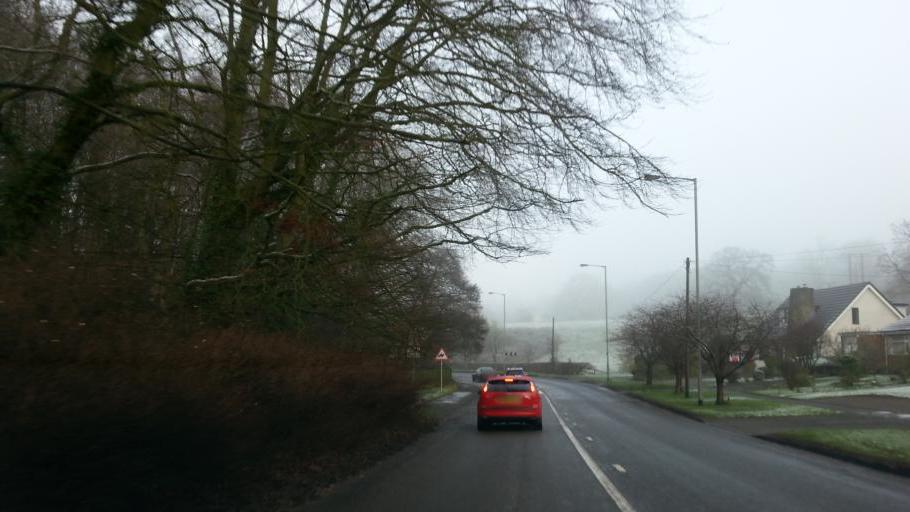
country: GB
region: England
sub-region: Staffordshire
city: Biddulph
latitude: 53.1318
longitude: -2.1659
